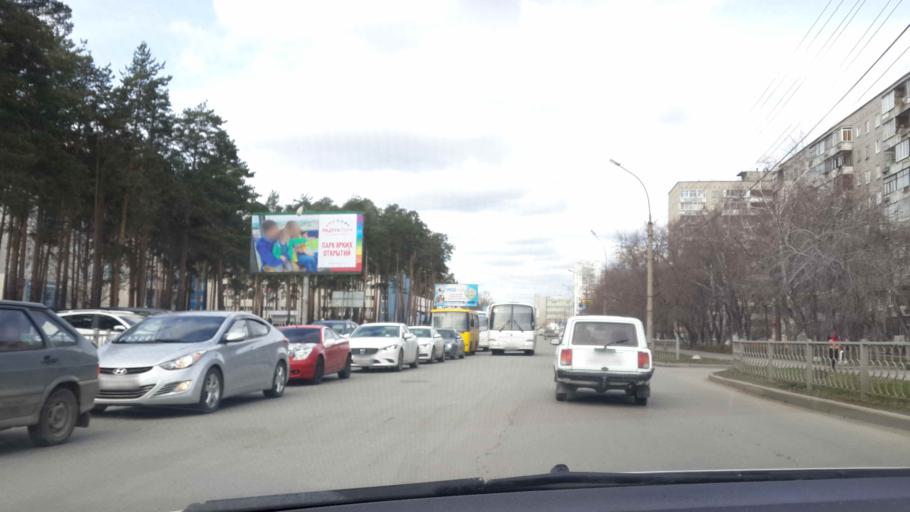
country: RU
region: Sverdlovsk
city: Sovkhoznyy
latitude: 56.8099
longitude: 60.5643
